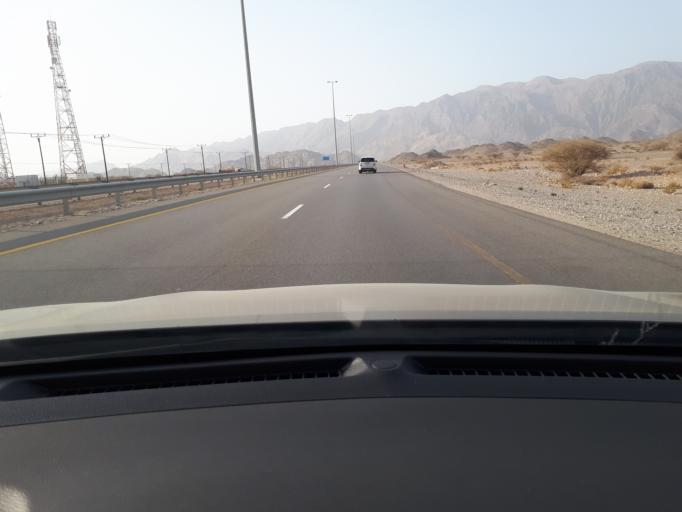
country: OM
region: Muhafazat Masqat
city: Muscat
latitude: 23.2926
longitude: 58.7417
